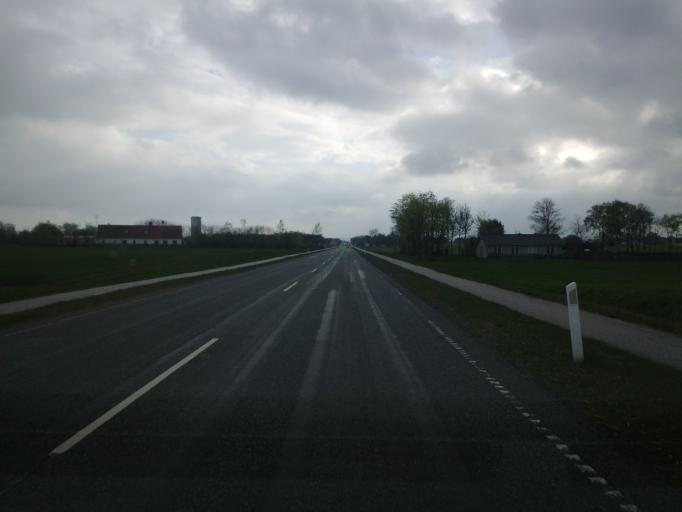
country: DK
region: North Denmark
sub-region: Frederikshavn Kommune
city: Saeby
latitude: 57.2932
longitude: 10.3929
